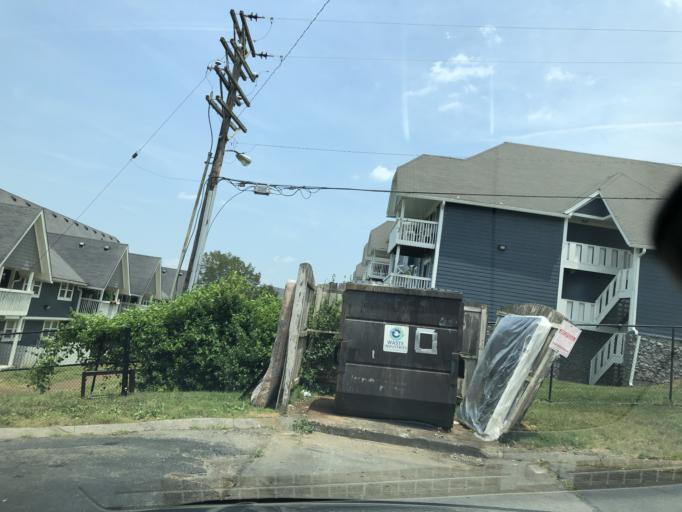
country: US
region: Tennessee
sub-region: Davidson County
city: Oak Hill
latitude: 36.0642
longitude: -86.6888
